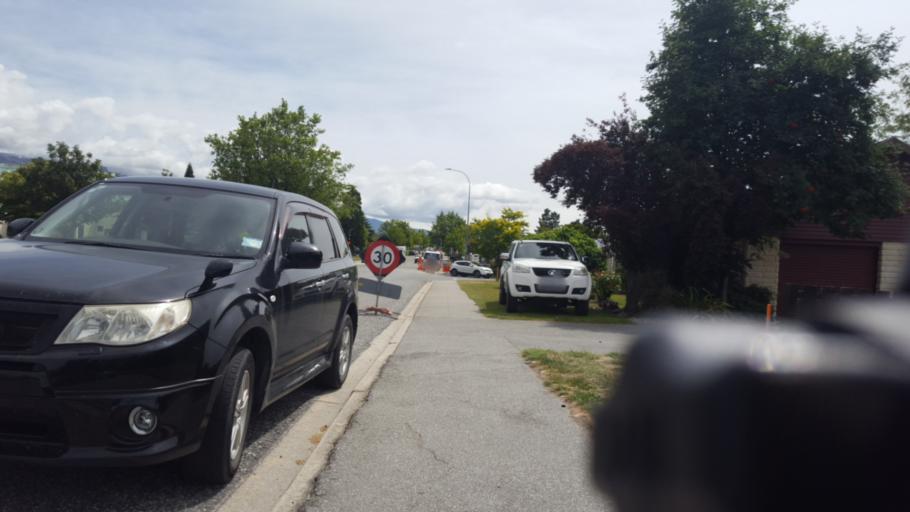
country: NZ
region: Otago
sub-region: Queenstown-Lakes District
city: Wanaka
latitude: -45.0399
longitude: 169.1979
